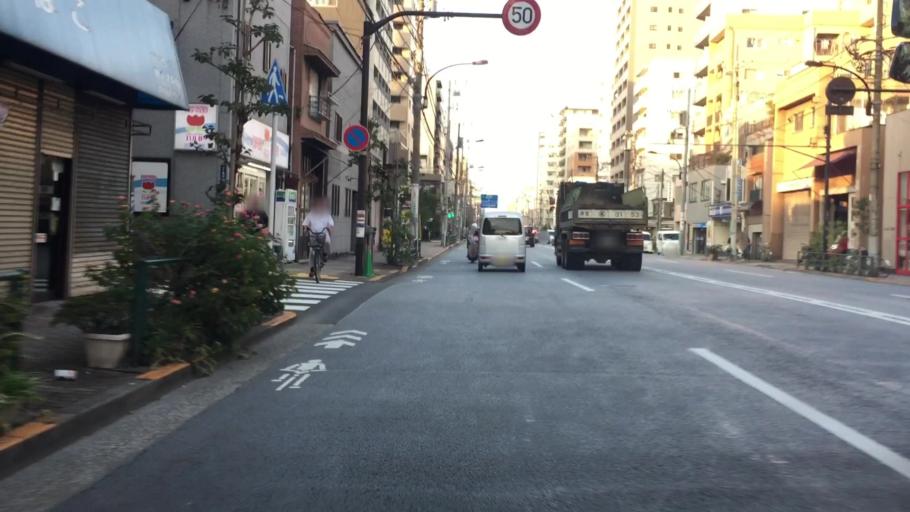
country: JP
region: Tokyo
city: Urayasu
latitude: 35.6982
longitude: 139.8052
